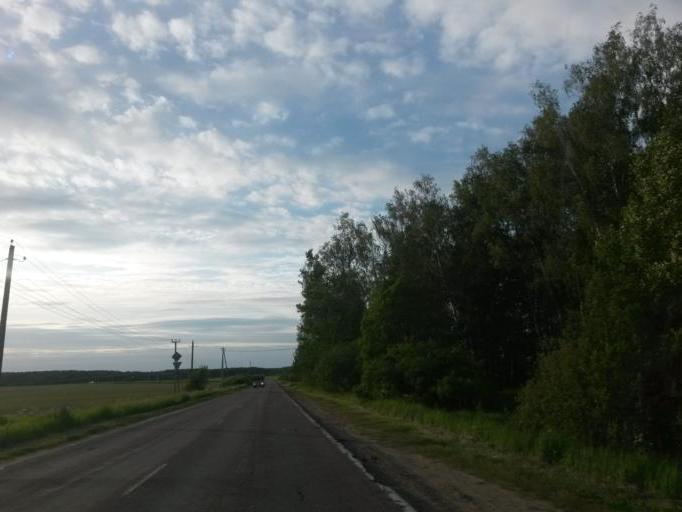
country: RU
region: Moskovskaya
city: Melikhovo
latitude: 55.1896
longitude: 37.7018
